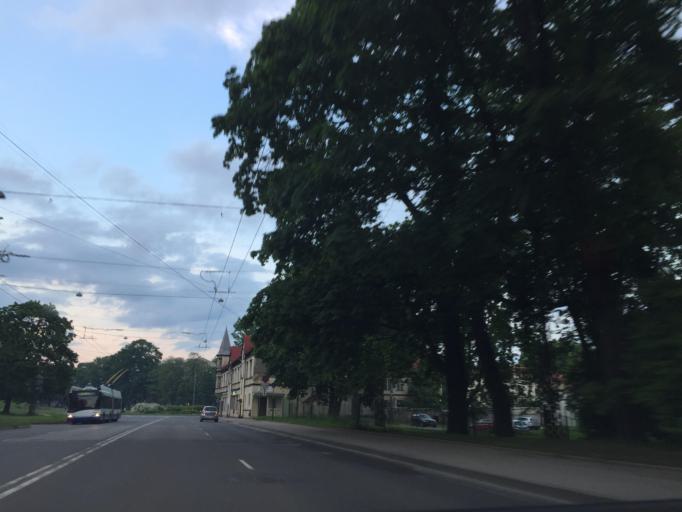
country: LV
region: Riga
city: Riga
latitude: 56.9644
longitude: 24.0560
